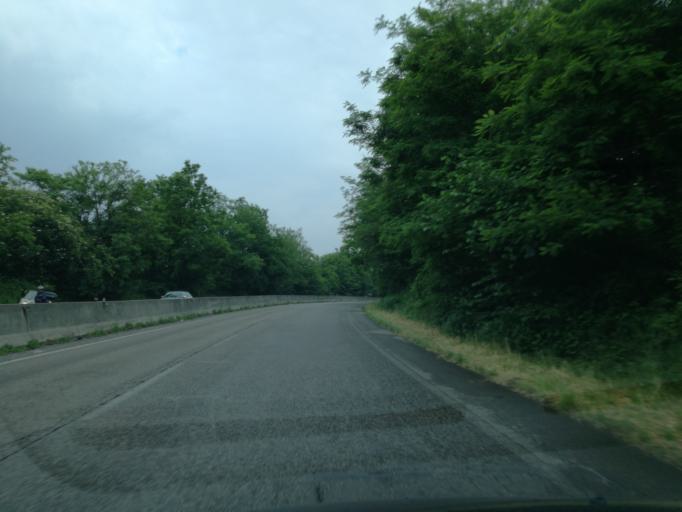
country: IT
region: Lombardy
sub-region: Provincia di Monza e Brianza
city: Villasanta
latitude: 45.6030
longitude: 9.3200
